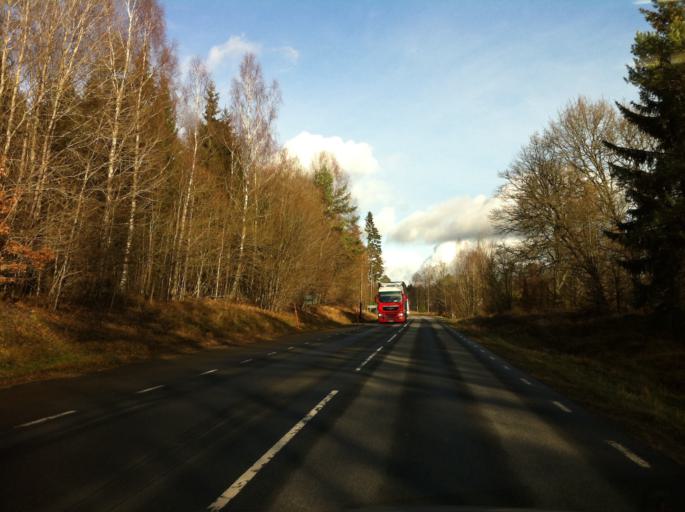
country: SE
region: Skane
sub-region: Osby Kommun
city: Osby
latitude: 56.4456
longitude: 14.0634
